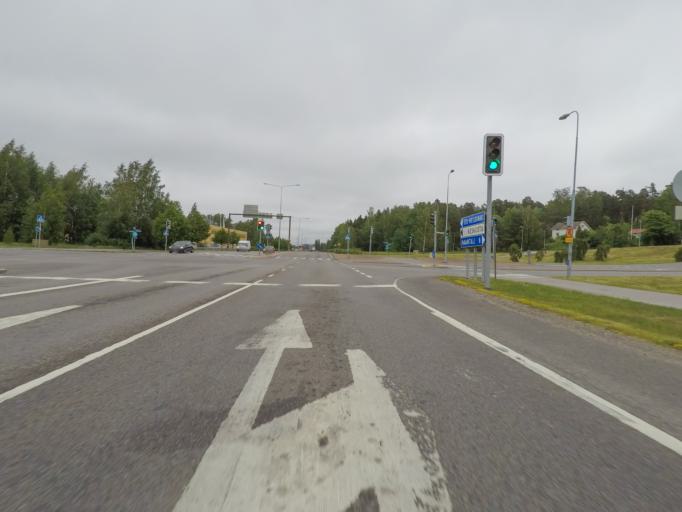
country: FI
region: Varsinais-Suomi
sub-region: Turku
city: Raisio
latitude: 60.4756
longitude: 22.1553
